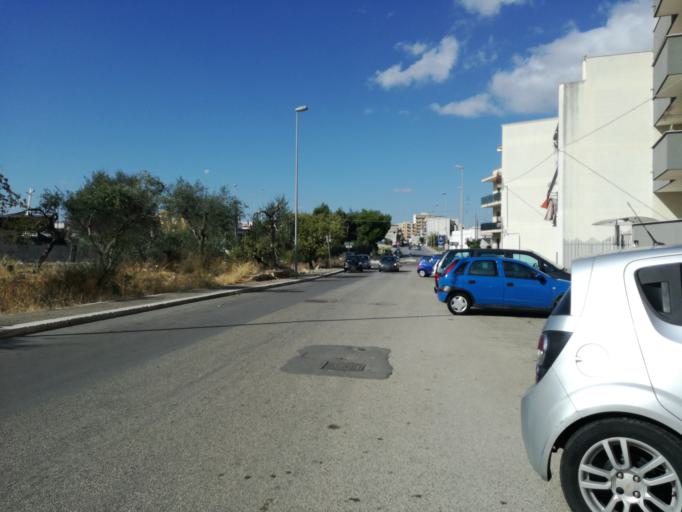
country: IT
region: Apulia
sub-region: Provincia di Bari
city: Triggiano
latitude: 41.0647
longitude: 16.9349
